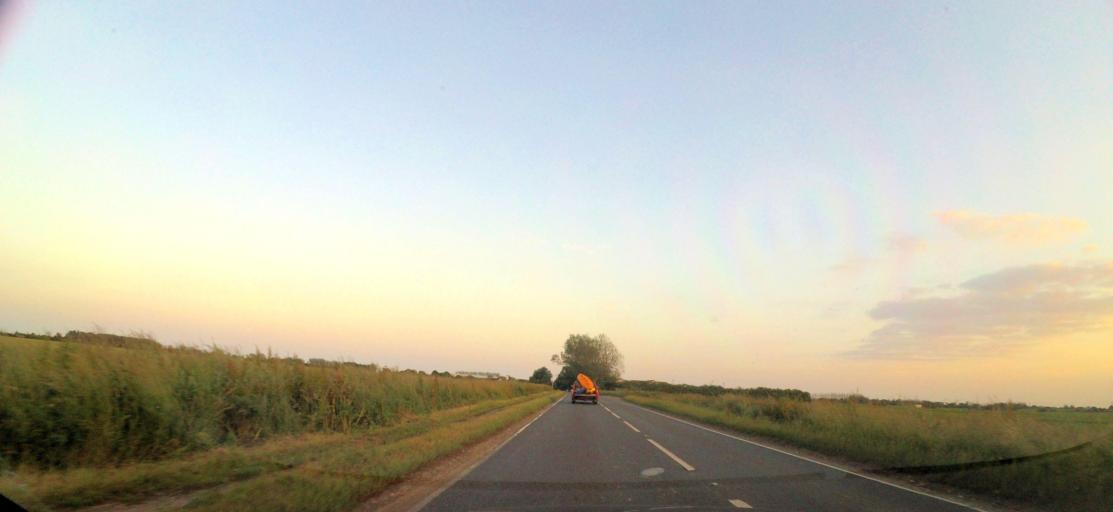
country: GB
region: England
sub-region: West Sussex
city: Selsey
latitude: 50.7507
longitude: -0.7820
